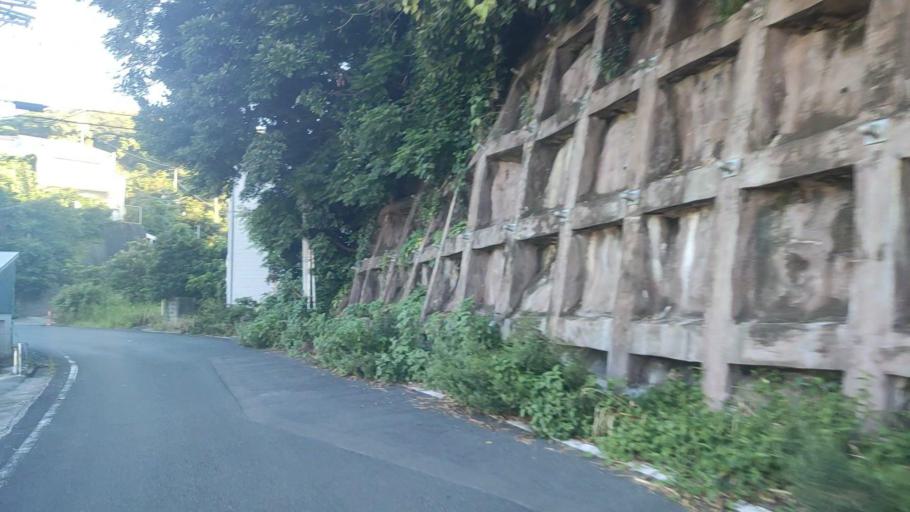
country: JP
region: Mie
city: Ise
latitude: 34.2734
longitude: 136.7645
